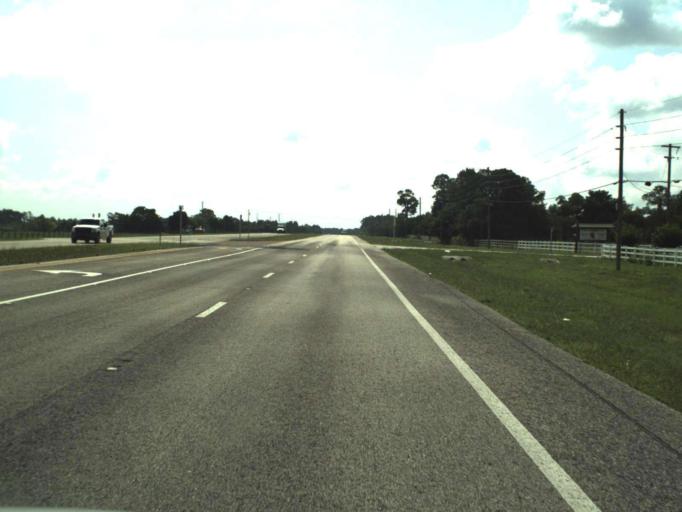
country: US
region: Florida
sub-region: Volusia County
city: Samsula-Spruce Creek
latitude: 29.0179
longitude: -81.1021
